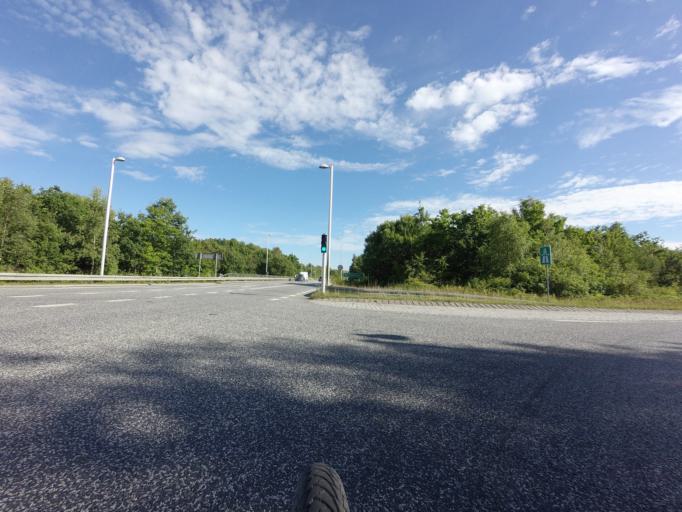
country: DK
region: Central Jutland
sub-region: Skanderborg Kommune
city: Stilling
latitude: 56.0673
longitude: 9.9769
